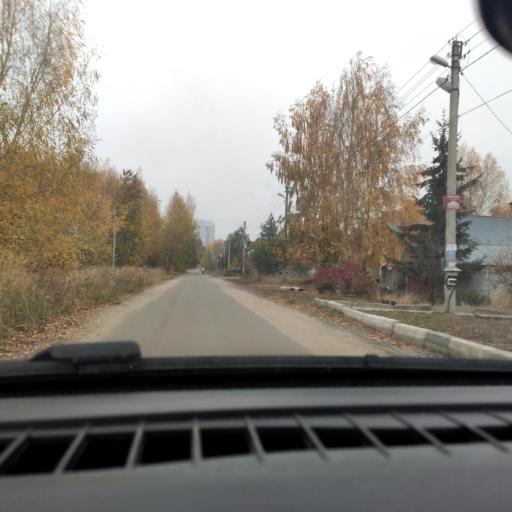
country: RU
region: Voronezj
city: Podgornoye
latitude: 51.7665
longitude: 39.1826
